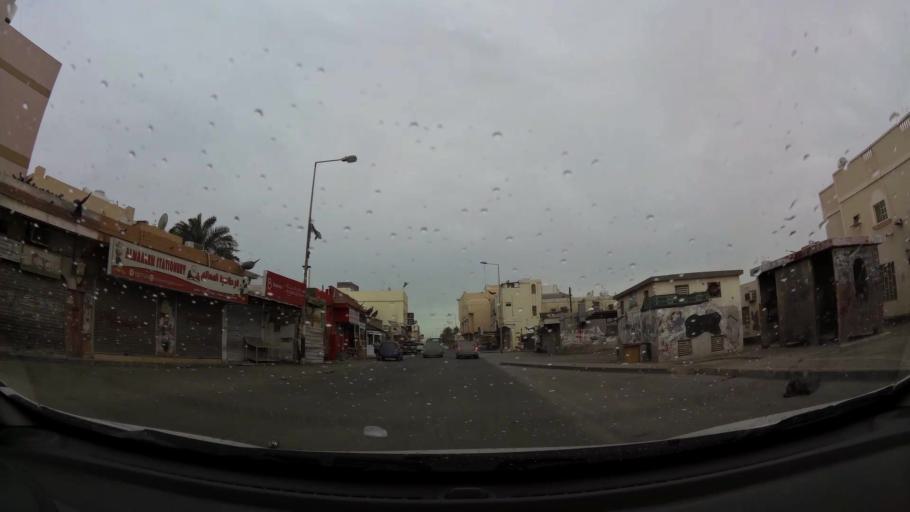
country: BH
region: Central Governorate
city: Madinat Hamad
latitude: 26.0981
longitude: 50.4859
